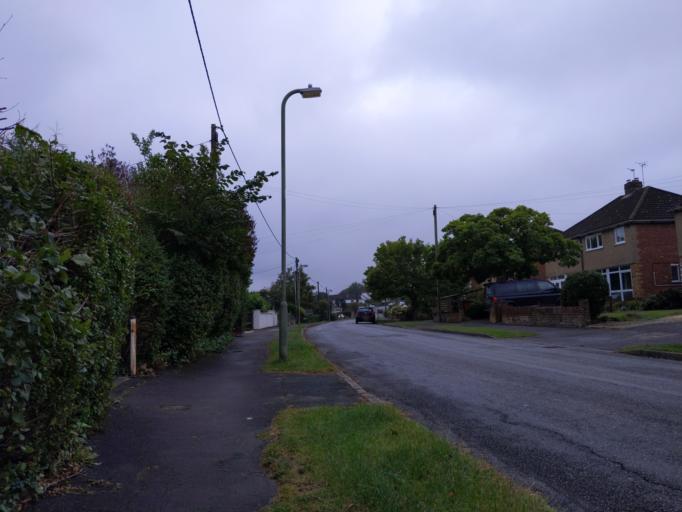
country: GB
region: England
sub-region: Oxfordshire
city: Oxford
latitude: 51.7206
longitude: -1.2482
